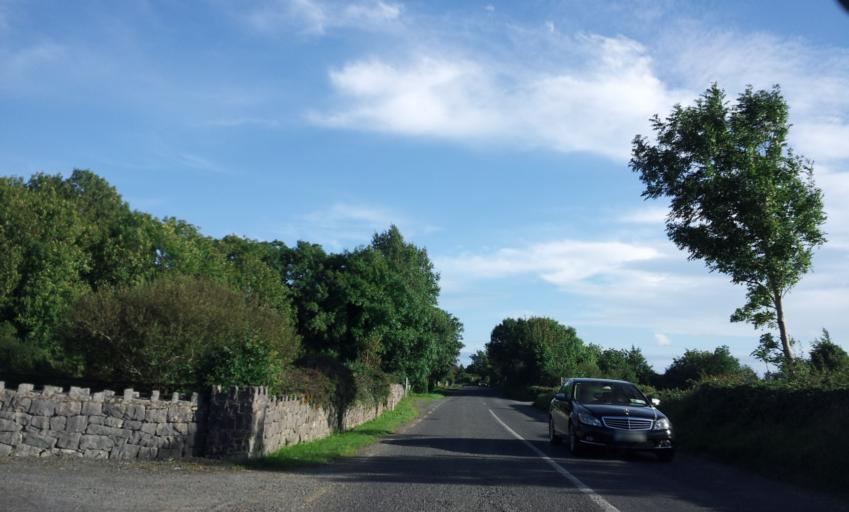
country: IE
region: Munster
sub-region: An Clar
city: Ennis
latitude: 52.9676
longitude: -9.0831
